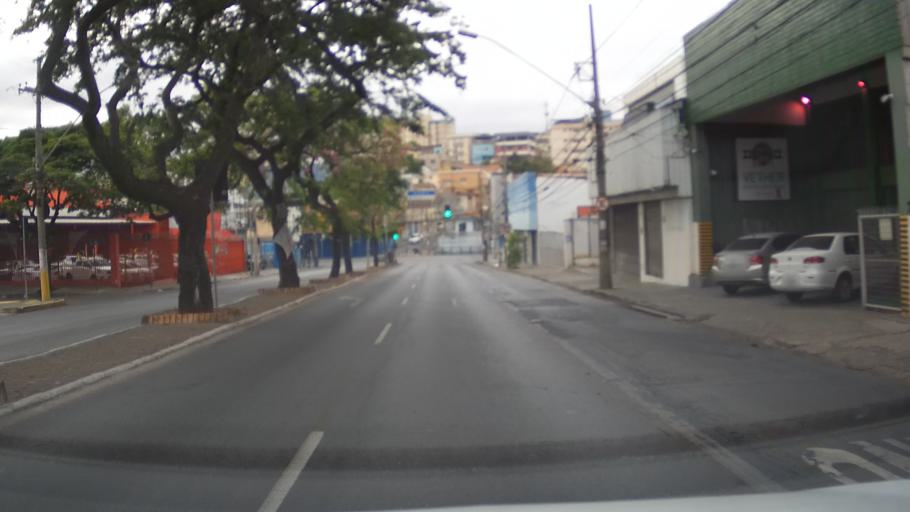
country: BR
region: Minas Gerais
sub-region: Belo Horizonte
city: Belo Horizonte
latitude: -19.9075
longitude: -43.9631
